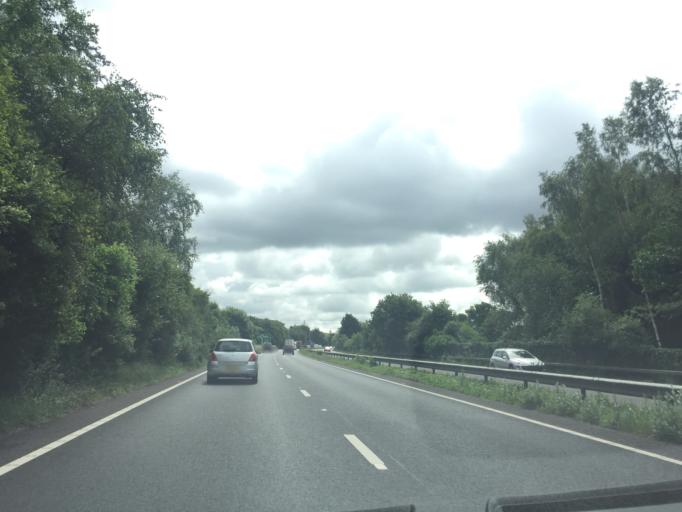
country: GB
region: England
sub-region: Dorset
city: Ferndown
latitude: 50.8146
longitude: -1.8783
